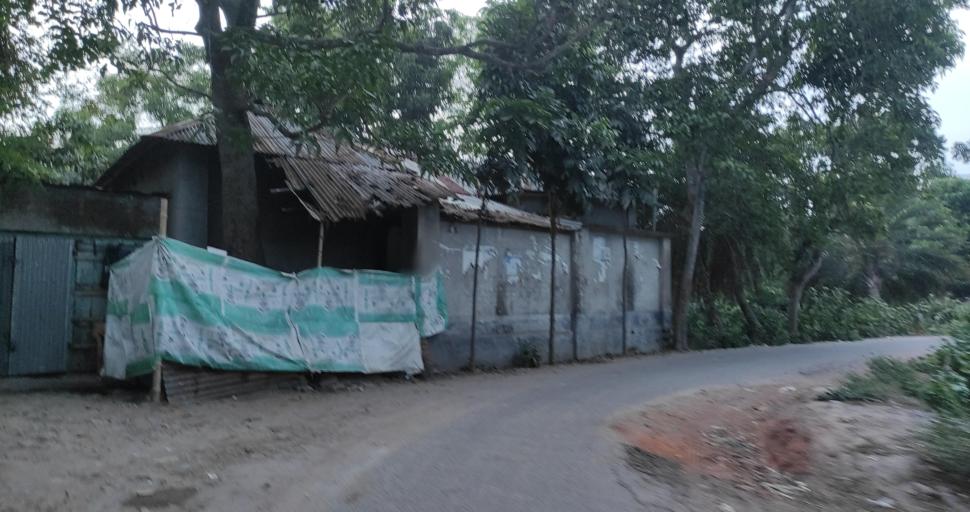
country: BD
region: Rajshahi
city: Par Naogaon
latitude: 24.5575
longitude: 88.9591
